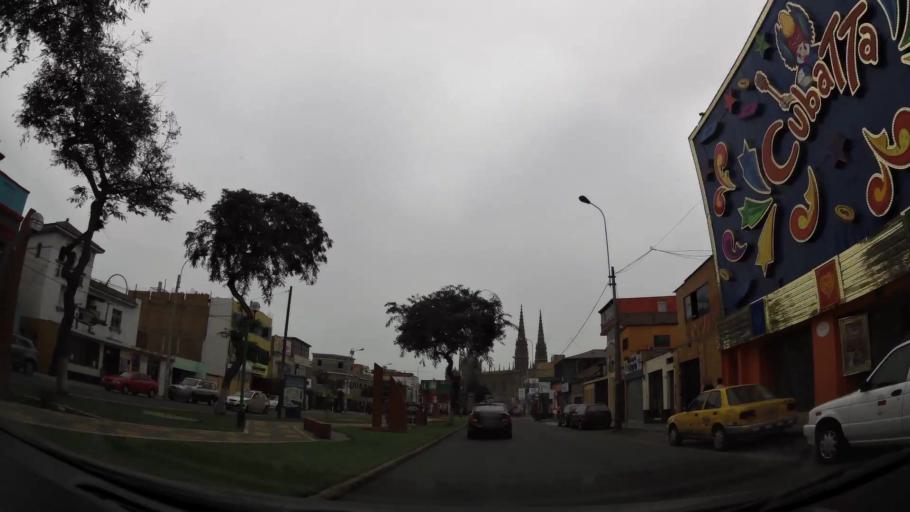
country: PE
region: Lima
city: Lima
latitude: -12.0750
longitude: -77.0462
